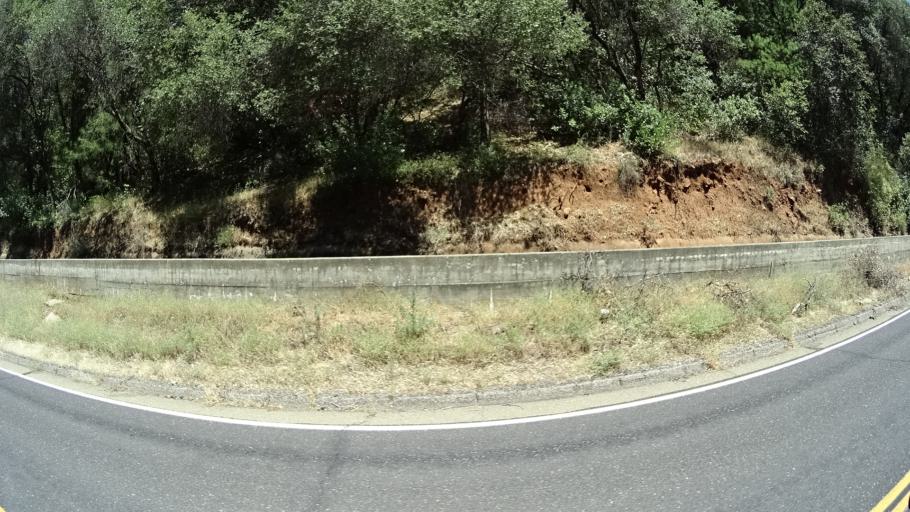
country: US
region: California
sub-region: Calaveras County
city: Murphys
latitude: 38.1311
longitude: -120.4854
